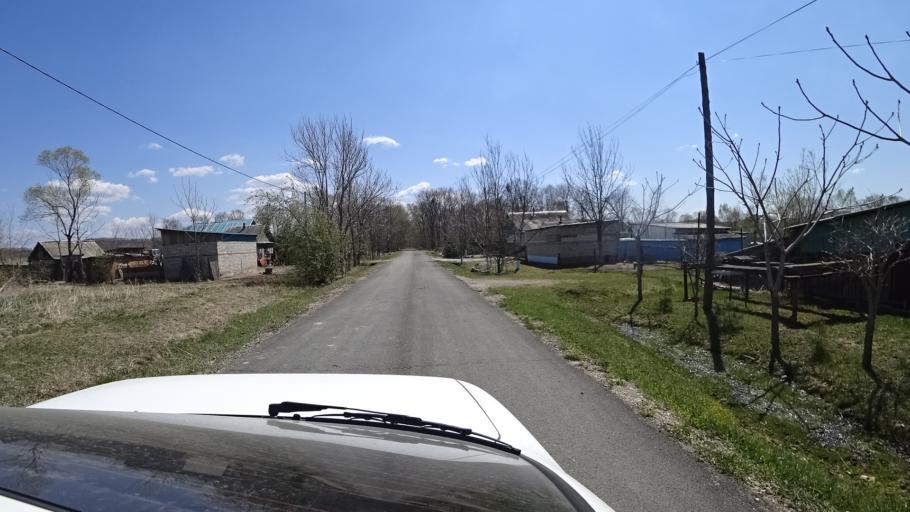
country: RU
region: Primorskiy
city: Dal'nerechensk
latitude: 45.7914
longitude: 133.7729
